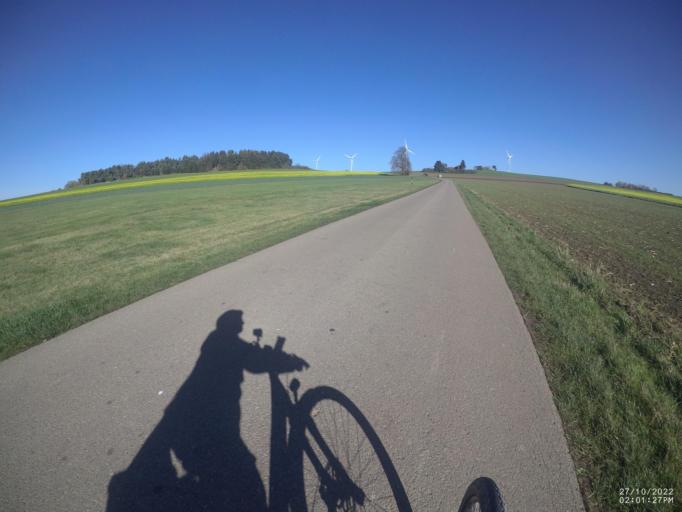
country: DE
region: Baden-Wuerttemberg
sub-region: Regierungsbezirk Stuttgart
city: Deggingen
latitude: 48.5705
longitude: 9.7380
